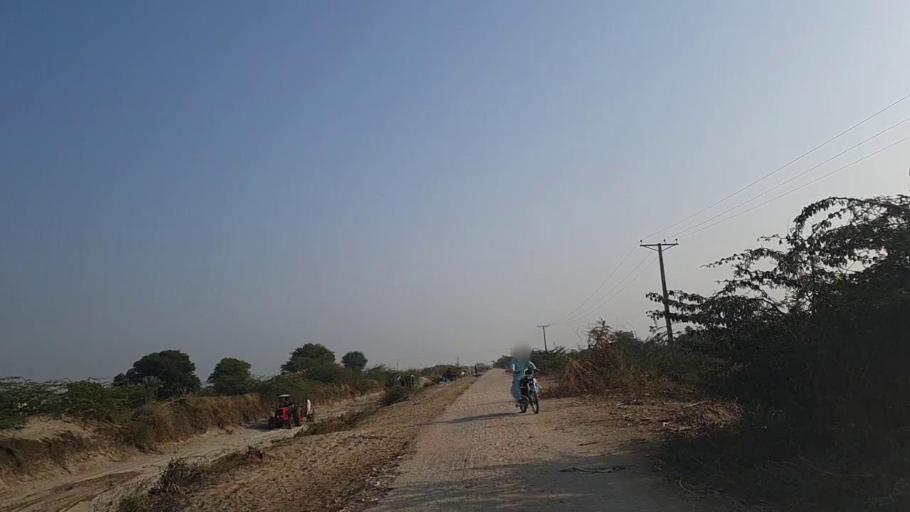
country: PK
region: Sindh
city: Jam Sahib
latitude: 26.2387
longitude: 68.5903
